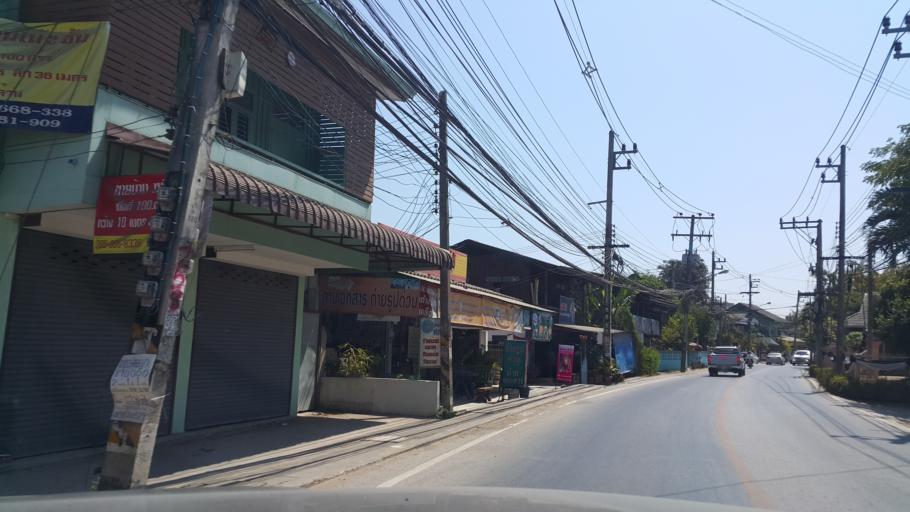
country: TH
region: Chiang Mai
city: San Sai
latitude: 18.8507
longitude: 99.0446
